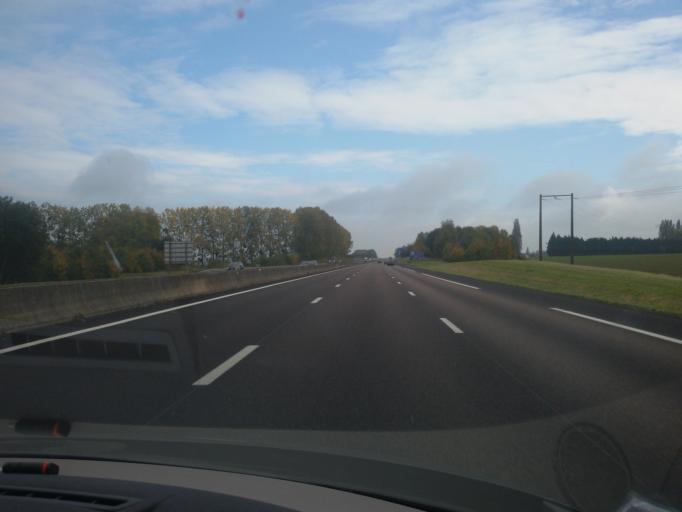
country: FR
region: Haute-Normandie
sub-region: Departement de l'Eure
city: Hauville
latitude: 49.3690
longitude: 0.7754
